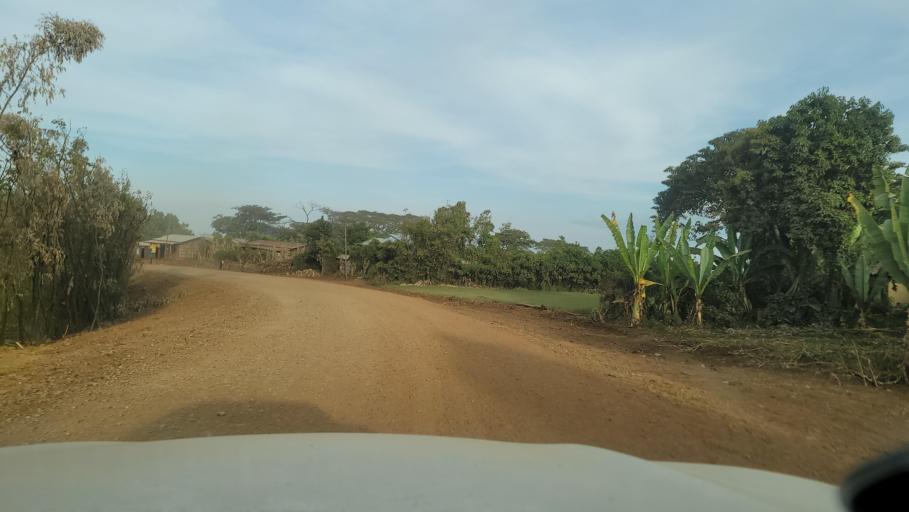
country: ET
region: Oromiya
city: Agaro
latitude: 7.8220
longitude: 36.5375
